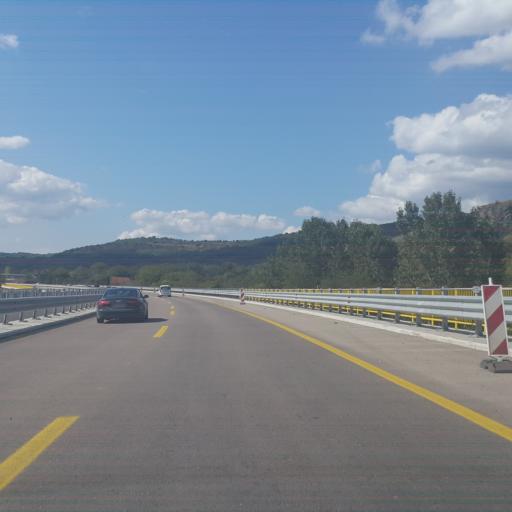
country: RS
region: Central Serbia
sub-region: Pirotski Okrug
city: Bela Palanka
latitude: 43.2344
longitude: 22.3755
